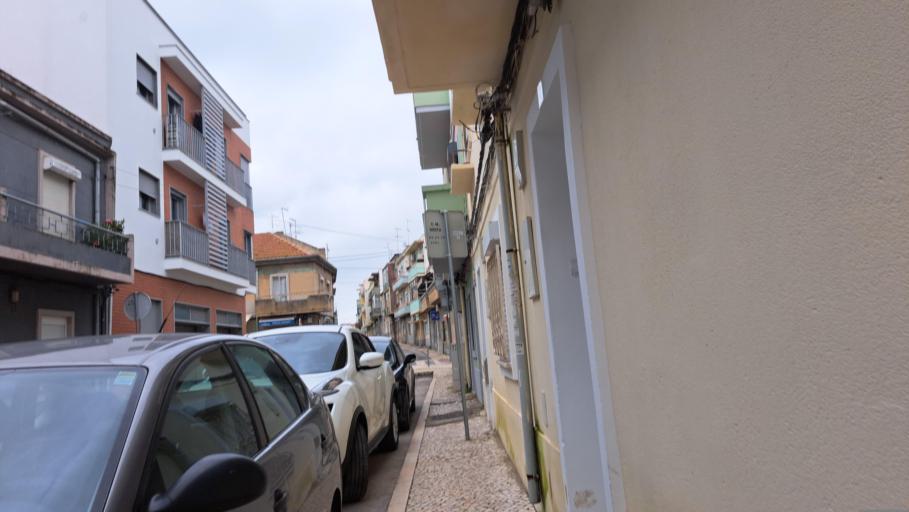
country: PT
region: Setubal
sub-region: Moita
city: Alhos Vedros
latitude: 38.6571
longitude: -9.0427
